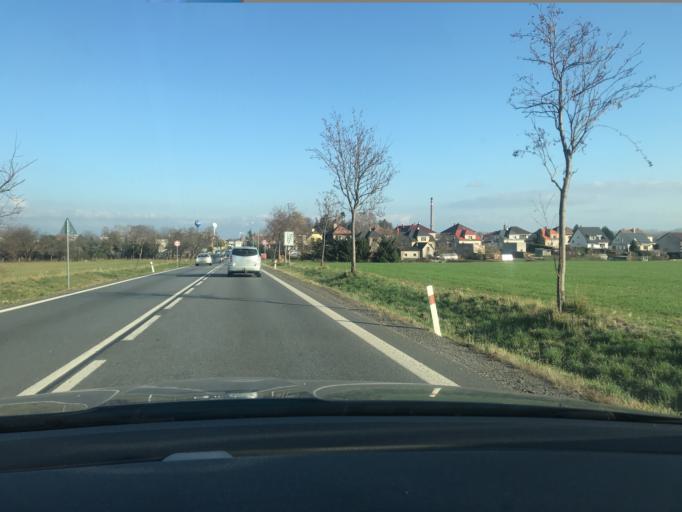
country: CZ
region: Kralovehradecky
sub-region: Okres Hradec Kralove
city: Smirice
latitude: 50.3052
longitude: 15.8544
